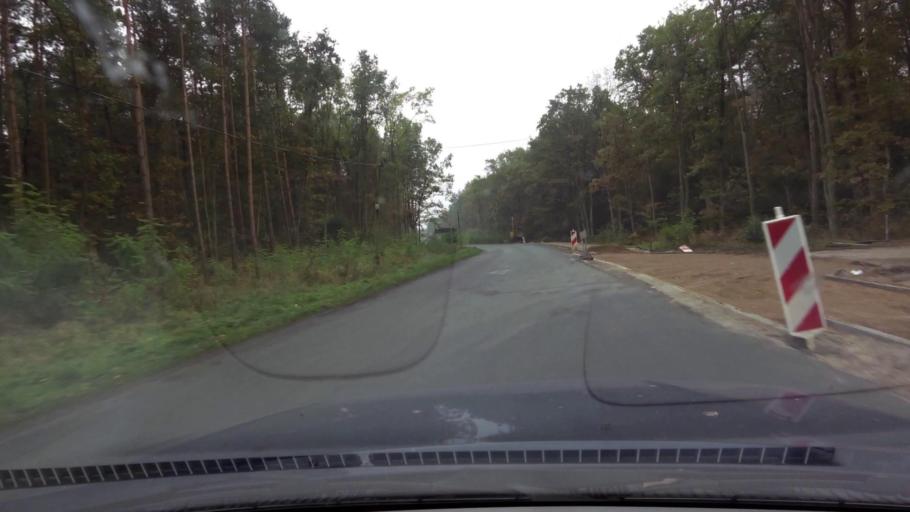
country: PL
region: West Pomeranian Voivodeship
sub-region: Powiat goleniowski
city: Goleniow
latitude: 53.5510
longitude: 14.7757
